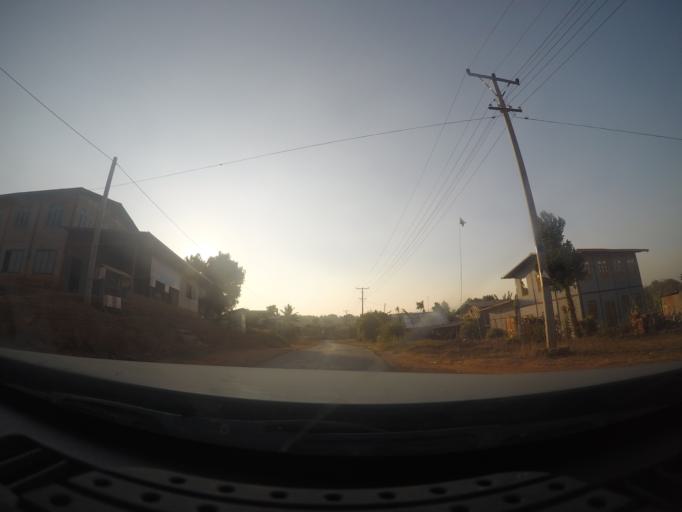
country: MM
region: Shan
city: Taunggyi
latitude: 20.4785
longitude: 97.1174
